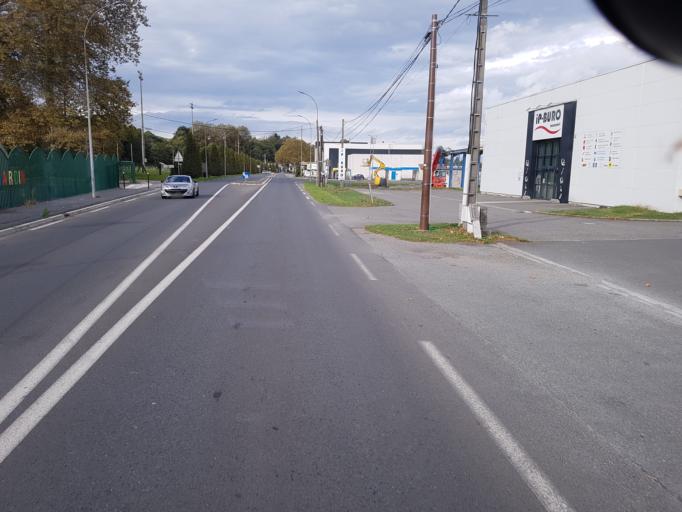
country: FR
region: Midi-Pyrenees
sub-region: Departement du Tarn
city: Pont-de-Larn
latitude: 43.4979
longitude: 2.3922
